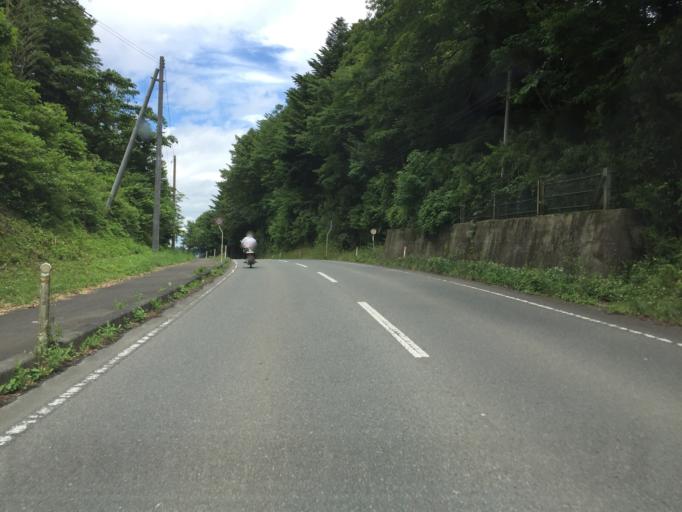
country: JP
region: Fukushima
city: Namie
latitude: 37.6882
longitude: 140.9693
